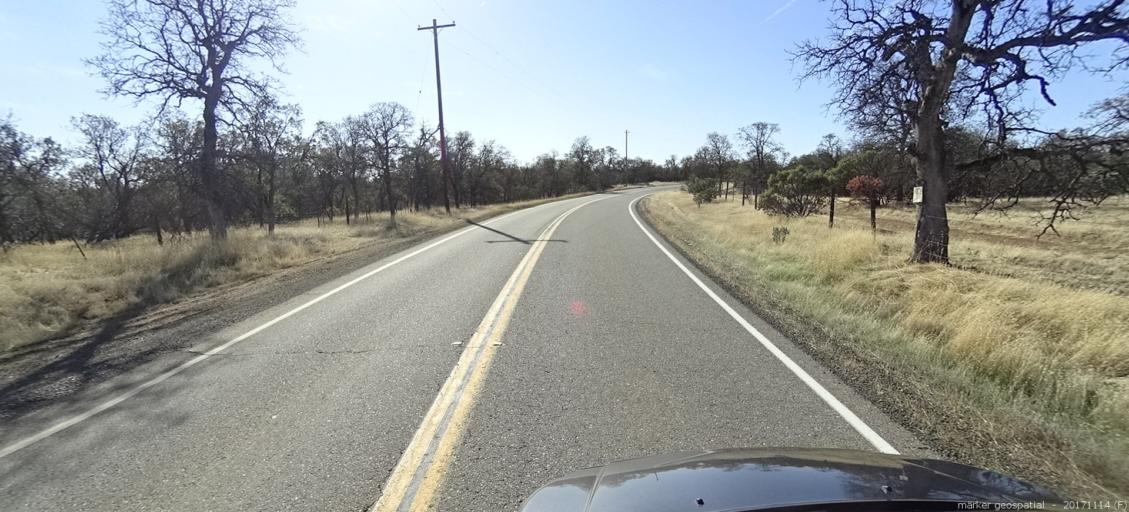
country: US
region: California
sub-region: Shasta County
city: Anderson
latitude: 40.4197
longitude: -122.3377
